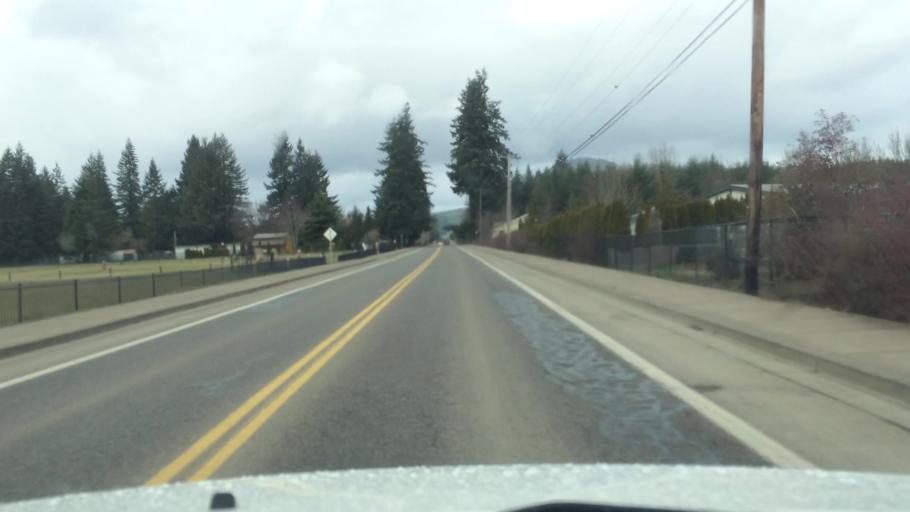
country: US
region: Oregon
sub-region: Polk County
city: Grand Ronde
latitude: 45.0675
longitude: -123.6119
